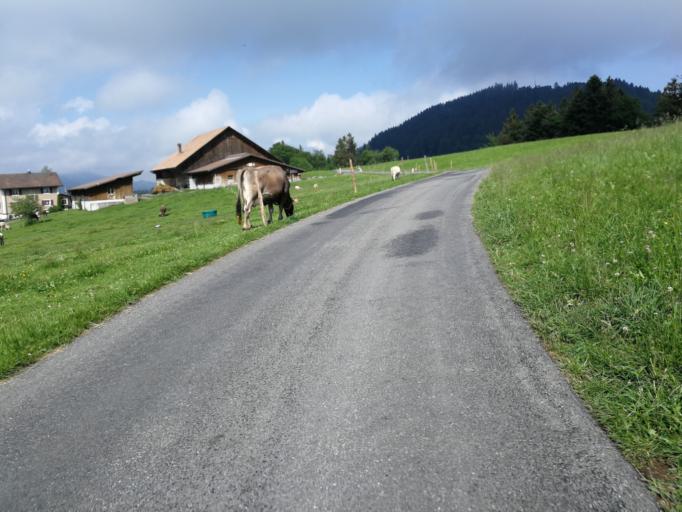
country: CH
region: Schwyz
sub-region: Bezirk Hoefe
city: Feusisberg
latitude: 47.1724
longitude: 8.7788
